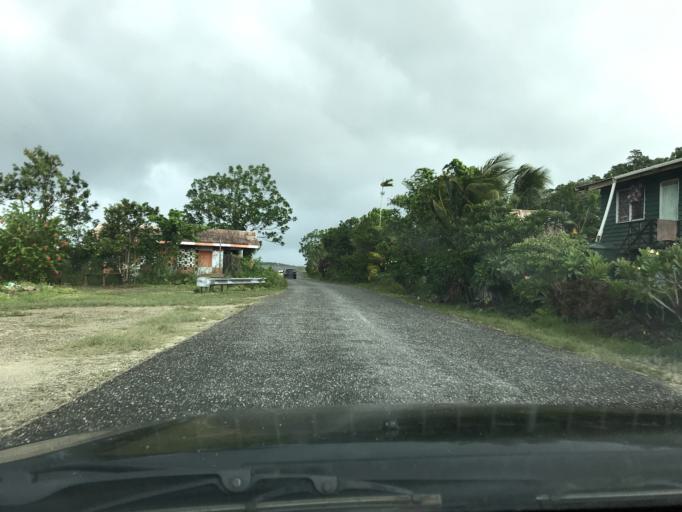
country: SB
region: Western Province
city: Gizo
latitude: -8.3253
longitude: 157.2669
